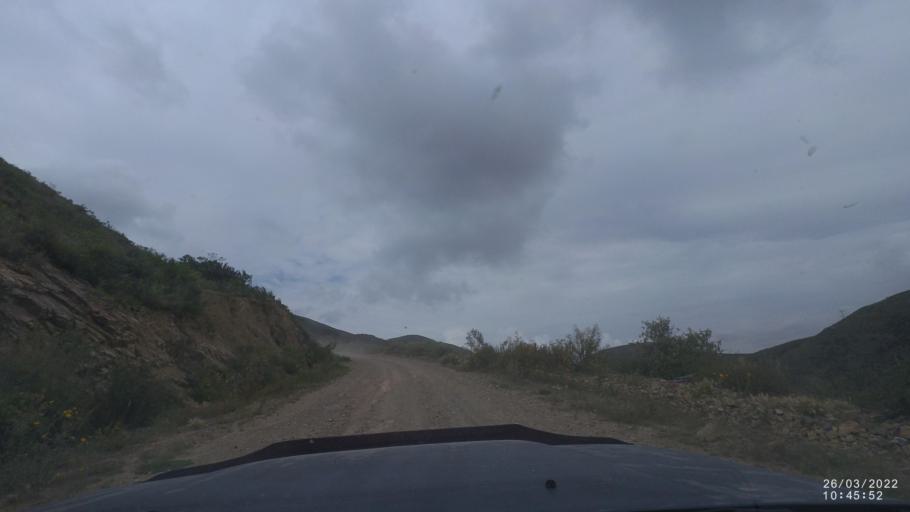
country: BO
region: Cochabamba
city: Tarata
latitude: -17.4826
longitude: -66.0499
